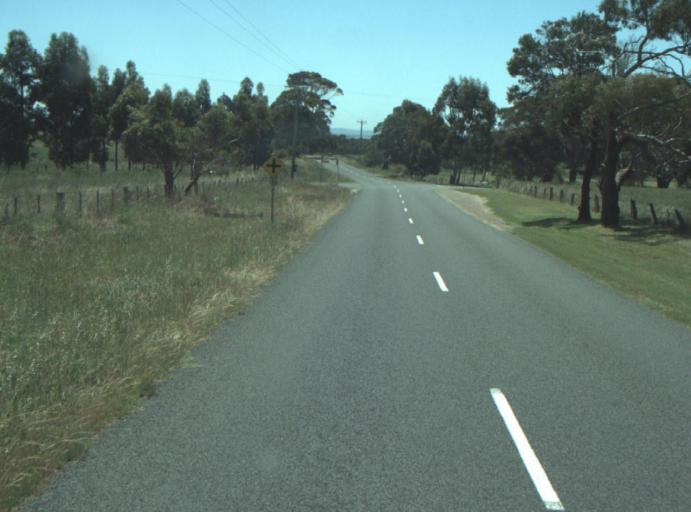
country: AU
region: Victoria
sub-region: Greater Geelong
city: Lara
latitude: -37.8738
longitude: 144.2719
